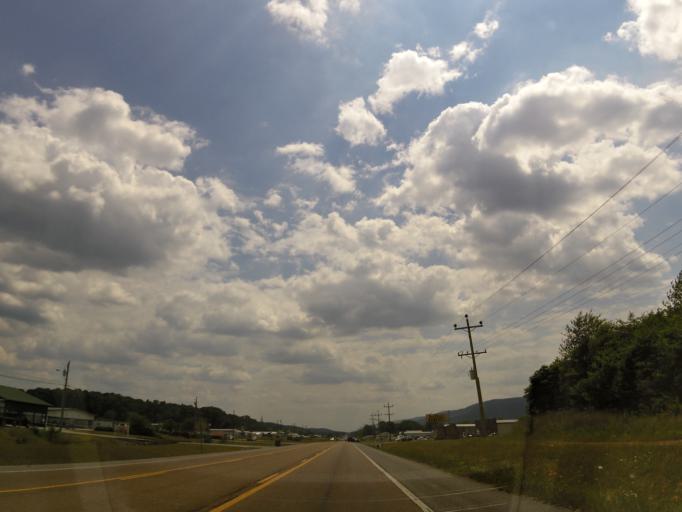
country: US
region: Tennessee
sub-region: Sequatchie County
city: Dunlap
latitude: 35.3473
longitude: -85.4069
